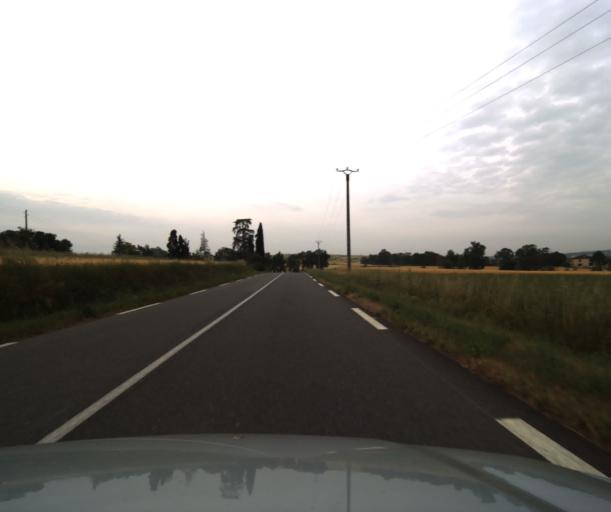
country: FR
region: Midi-Pyrenees
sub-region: Departement du Gers
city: Aubiet
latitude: 43.6663
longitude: 0.7984
